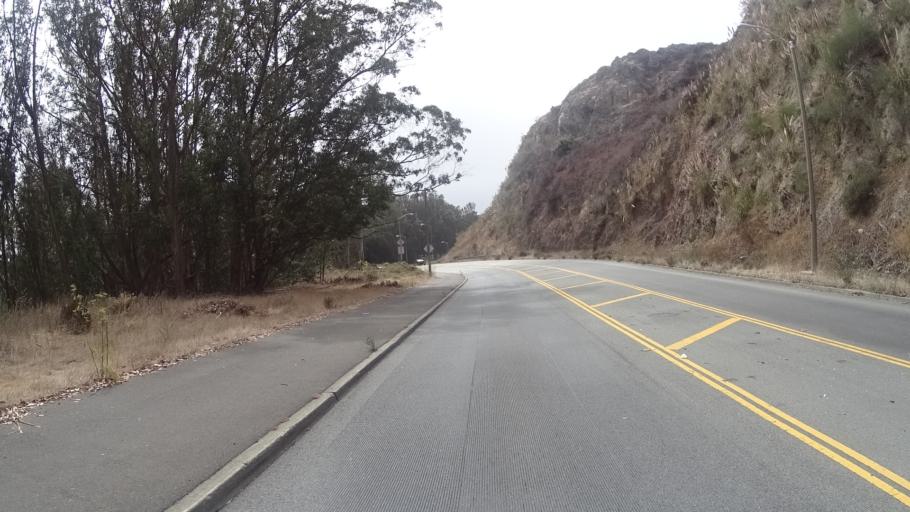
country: US
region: California
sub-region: San Mateo County
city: Daly City
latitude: 37.7391
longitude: -122.4425
